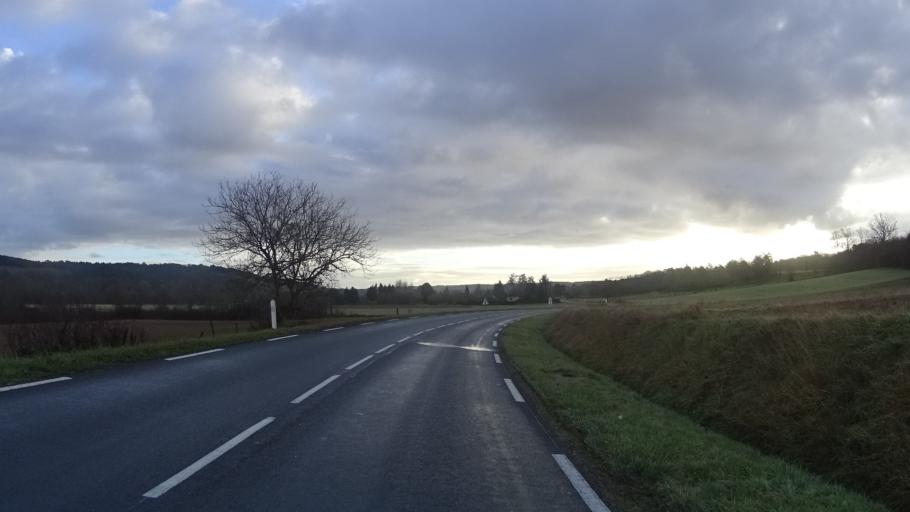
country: FR
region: Aquitaine
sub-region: Departement de la Dordogne
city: Bassillac
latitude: 45.1927
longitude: 0.8303
